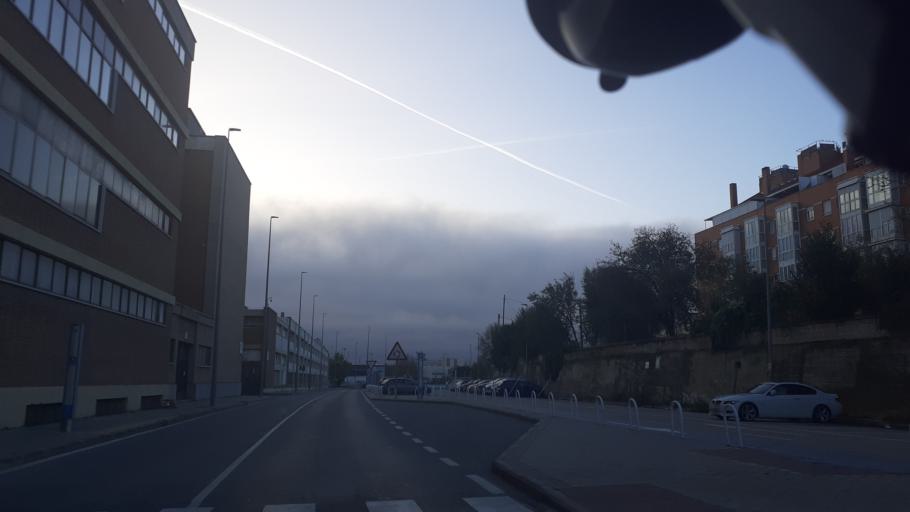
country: ES
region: Madrid
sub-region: Provincia de Madrid
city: Barajas de Madrid
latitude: 40.4764
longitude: -3.5757
